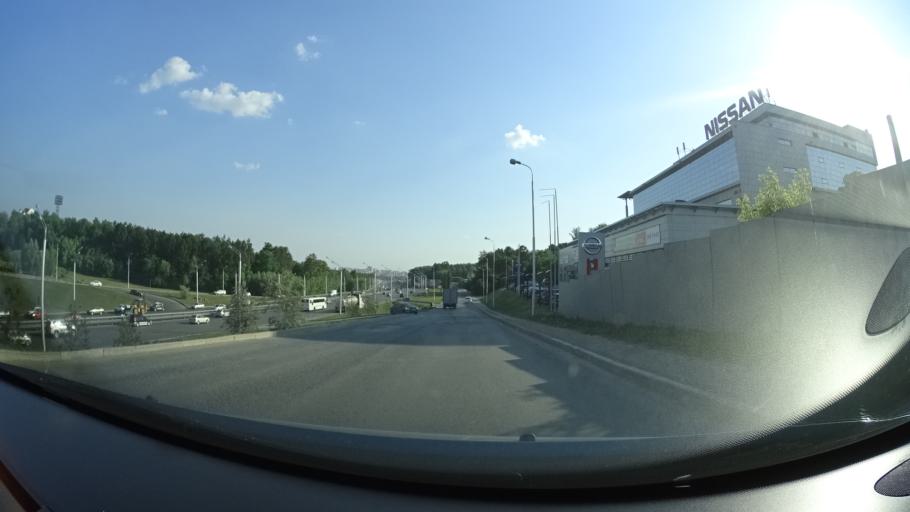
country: RU
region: Bashkortostan
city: Ufa
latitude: 54.7504
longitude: 56.0157
